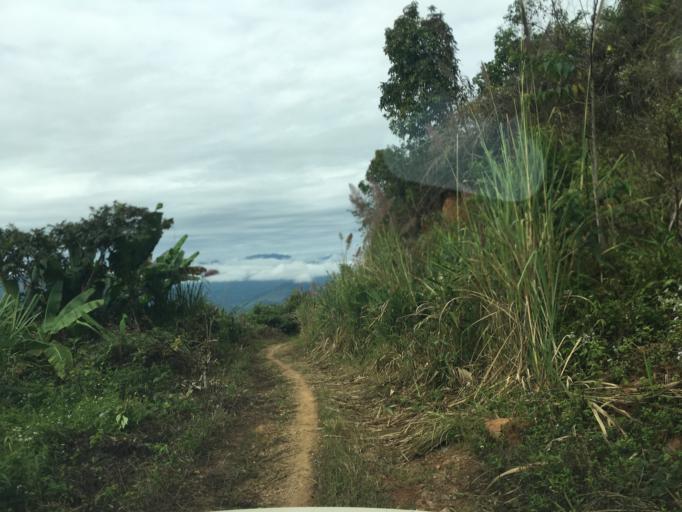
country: LA
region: Houaphan
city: Viengthong
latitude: 19.9173
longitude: 103.2990
